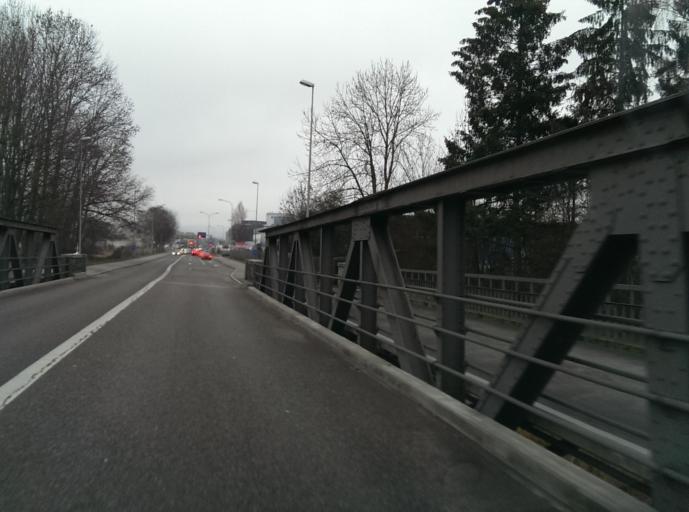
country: CH
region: Zurich
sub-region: Bezirk Dietikon
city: Schlieren / Spital
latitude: 47.4021
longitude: 8.4339
